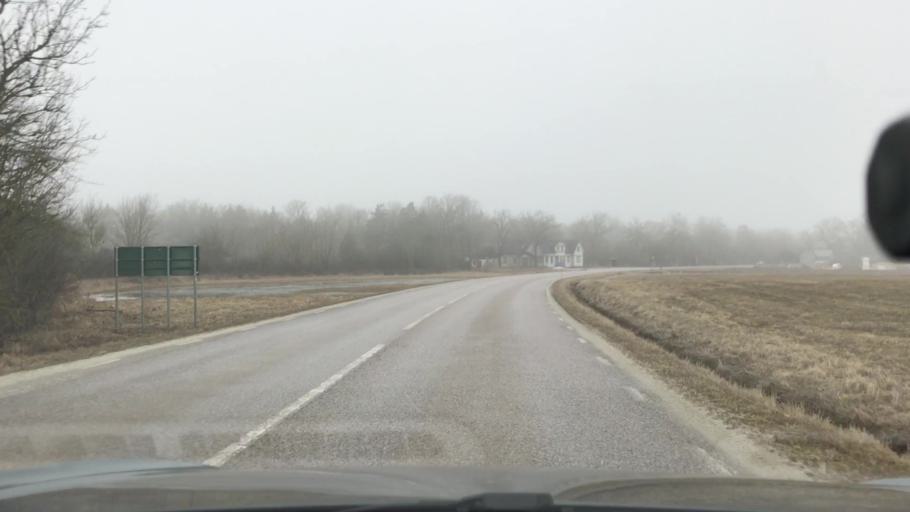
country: SE
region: Gotland
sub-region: Gotland
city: Hemse
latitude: 57.3076
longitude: 18.3800
